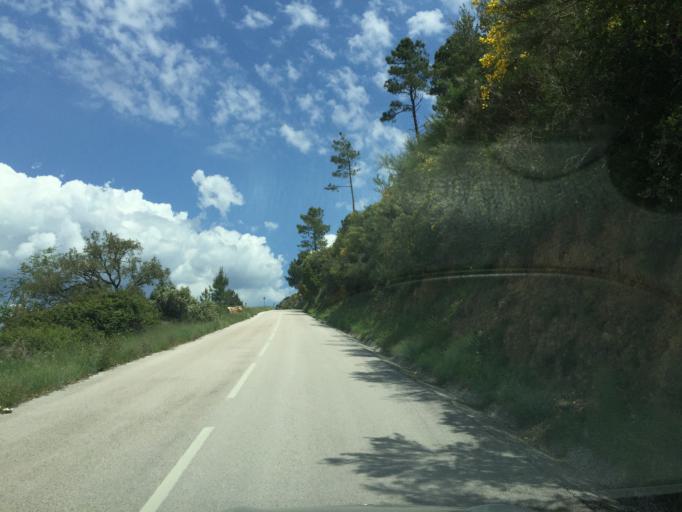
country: PT
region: Coimbra
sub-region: Pampilhosa da Serra
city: Pampilhosa da Serra
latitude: 40.0847
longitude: -7.8590
